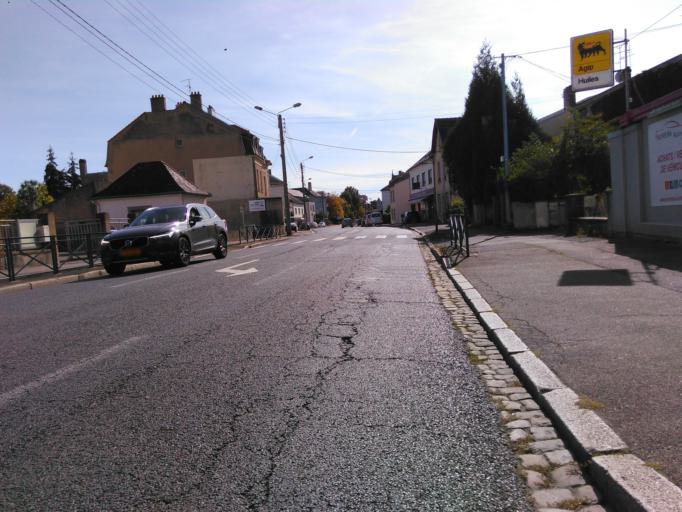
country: FR
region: Lorraine
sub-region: Departement de la Moselle
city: Thionville
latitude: 49.3693
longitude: 6.1691
